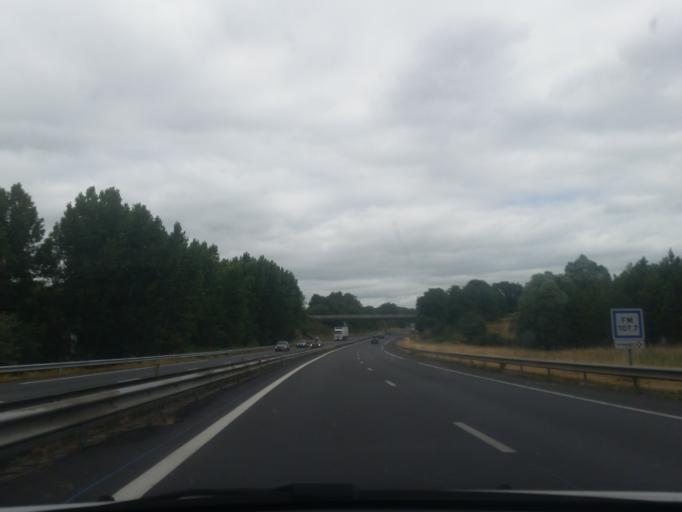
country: FR
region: Pays de la Loire
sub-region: Departement de Maine-et-Loire
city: Seiches-sur-le-Loir
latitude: 47.5776
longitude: -0.3348
